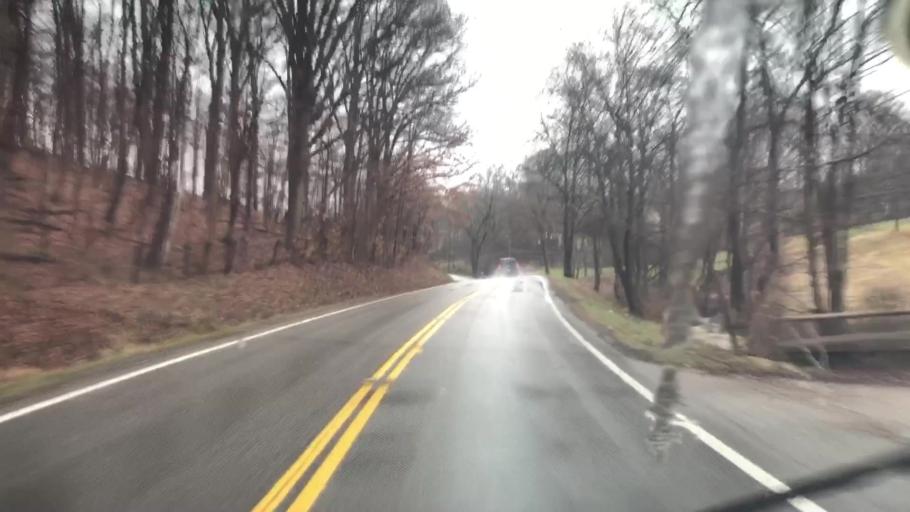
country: US
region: Ohio
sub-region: Belmont County
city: Saint Clairsville
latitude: 40.1003
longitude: -80.9189
